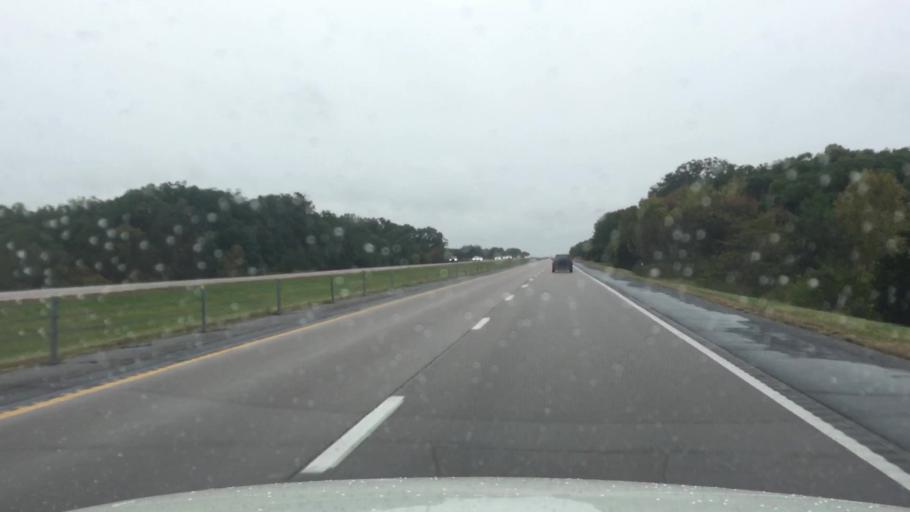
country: US
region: Missouri
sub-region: Boone County
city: Ashland
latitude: 38.7273
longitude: -92.2543
